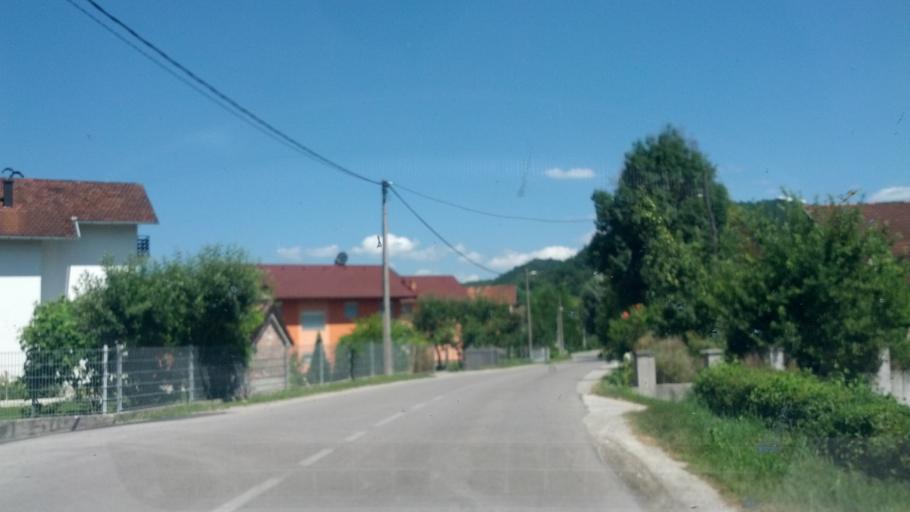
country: BA
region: Federation of Bosnia and Herzegovina
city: Otoka
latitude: 44.9720
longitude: 16.1795
